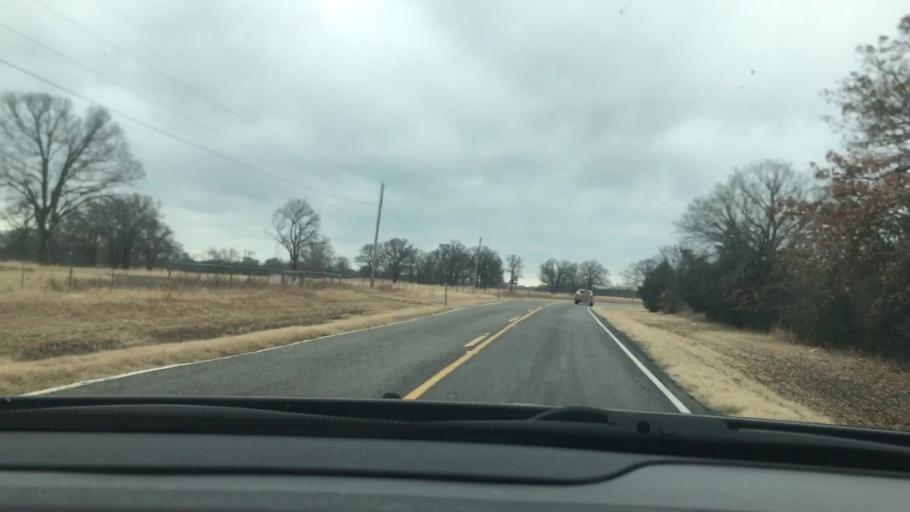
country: US
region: Oklahoma
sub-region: Johnston County
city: Tishomingo
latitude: 34.1876
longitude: -96.5793
